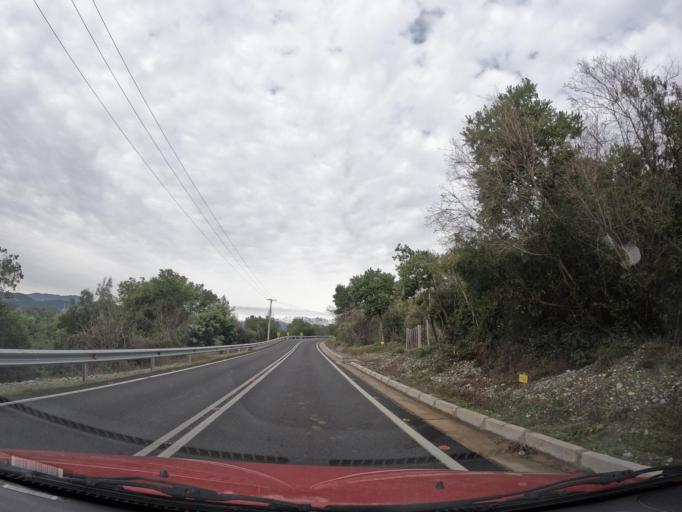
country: CL
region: Maule
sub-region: Provincia de Linares
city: Linares
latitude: -35.9196
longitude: -71.4578
